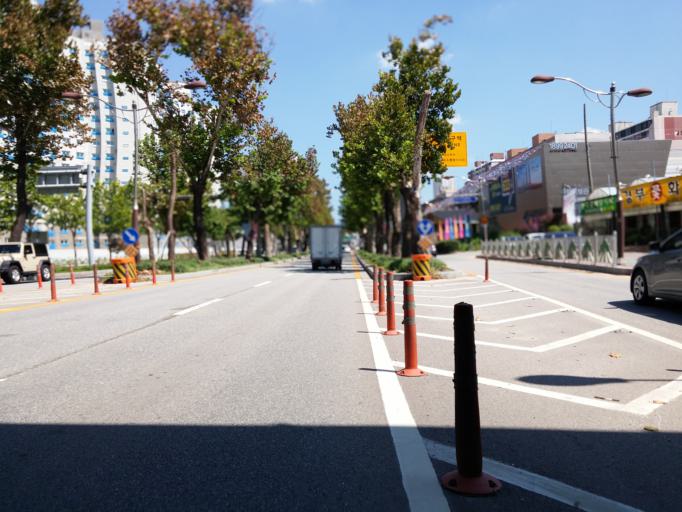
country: KR
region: Chungcheongbuk-do
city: Cheongju-si
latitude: 36.6262
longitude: 127.4205
